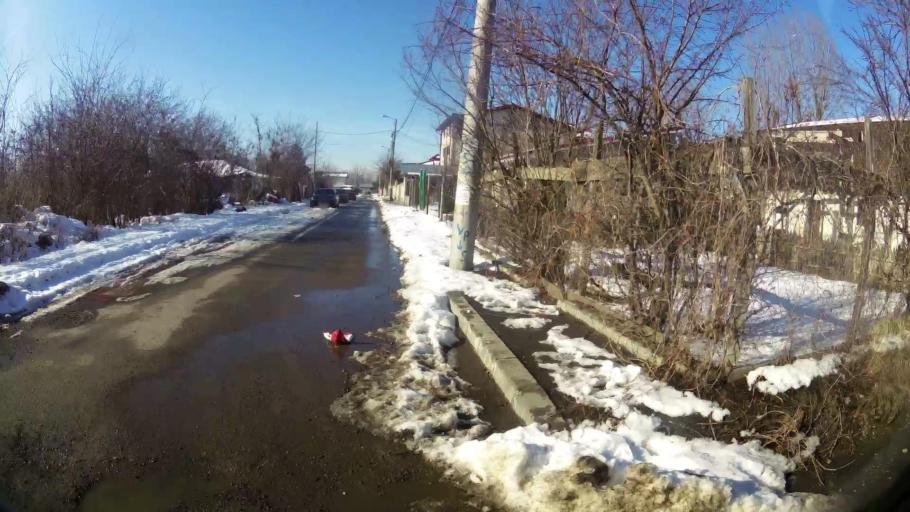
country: RO
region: Ilfov
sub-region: Comuna Magurele
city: Magurele
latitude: 44.3880
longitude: 26.0530
